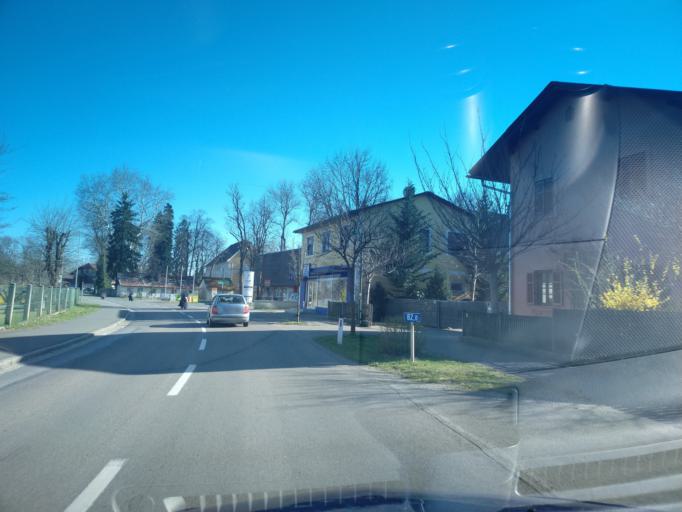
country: AT
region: Styria
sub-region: Politischer Bezirk Leibnitz
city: Stocking
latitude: 46.8567
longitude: 15.5361
